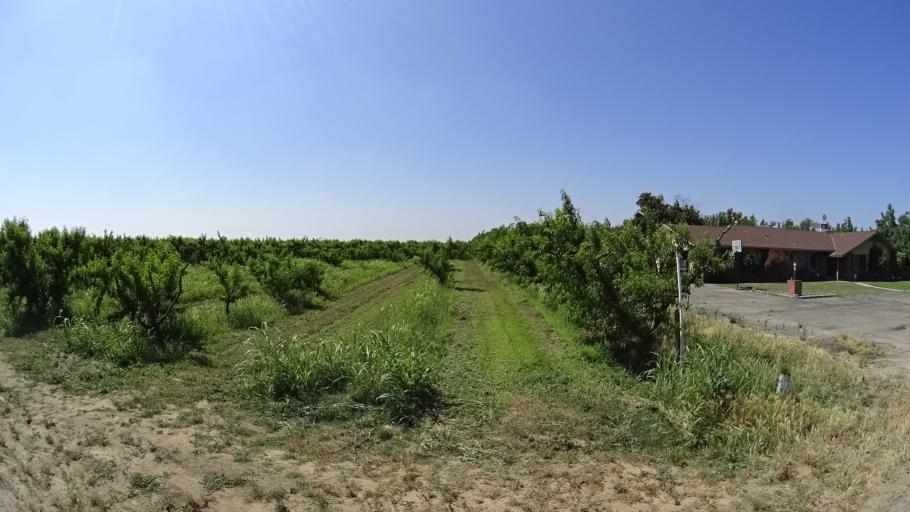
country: US
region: California
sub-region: Fresno County
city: Kingsburg
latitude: 36.4596
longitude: -119.5633
